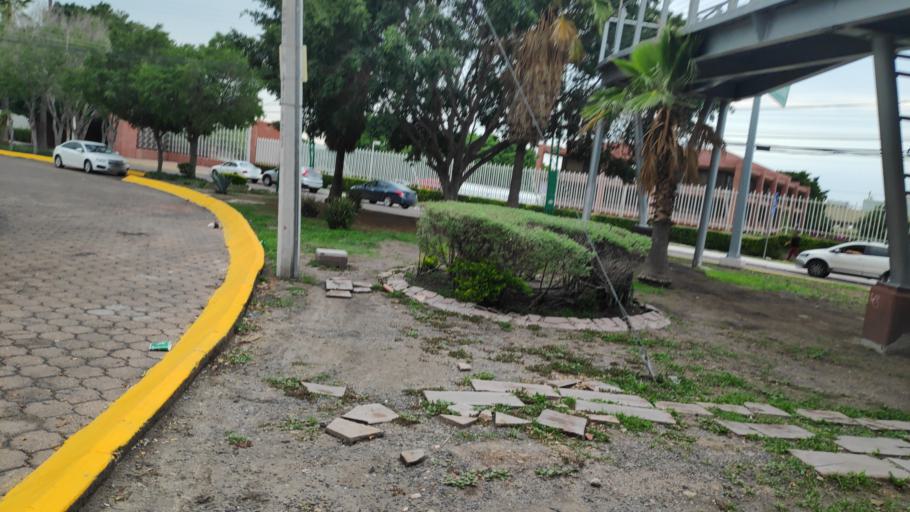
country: MX
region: Queretaro
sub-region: Queretaro
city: Santiago de Queretaro
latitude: 20.5876
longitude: -100.3701
